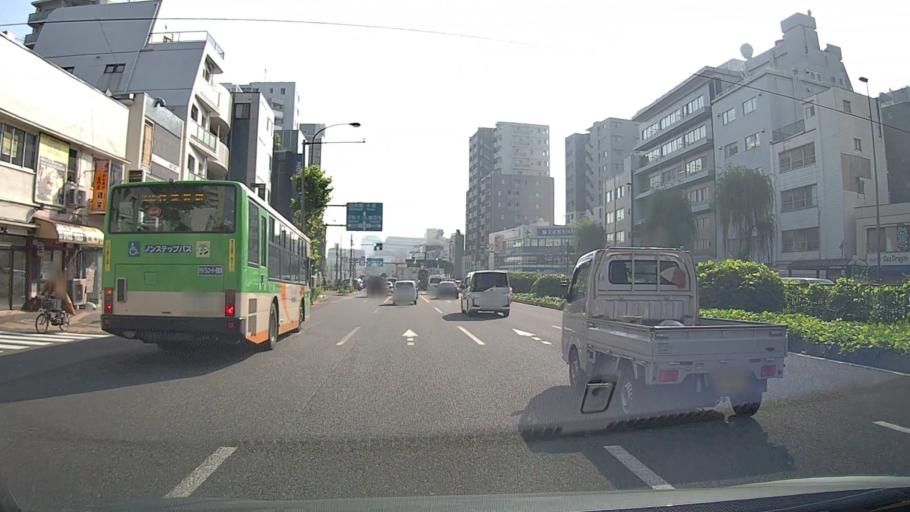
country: JP
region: Tokyo
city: Tokyo
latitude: 35.7294
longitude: 139.7431
